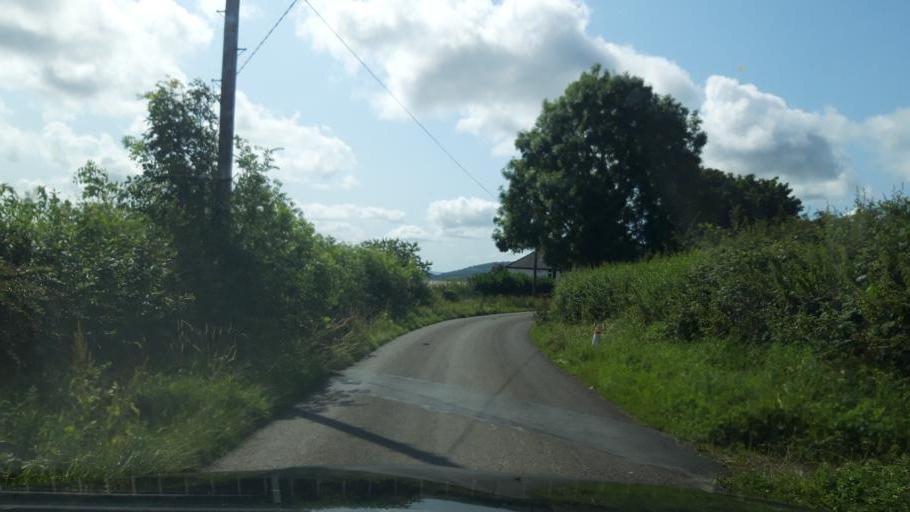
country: IE
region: Leinster
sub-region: Kilkenny
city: Graiguenamanagh
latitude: 52.5683
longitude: -6.9795
